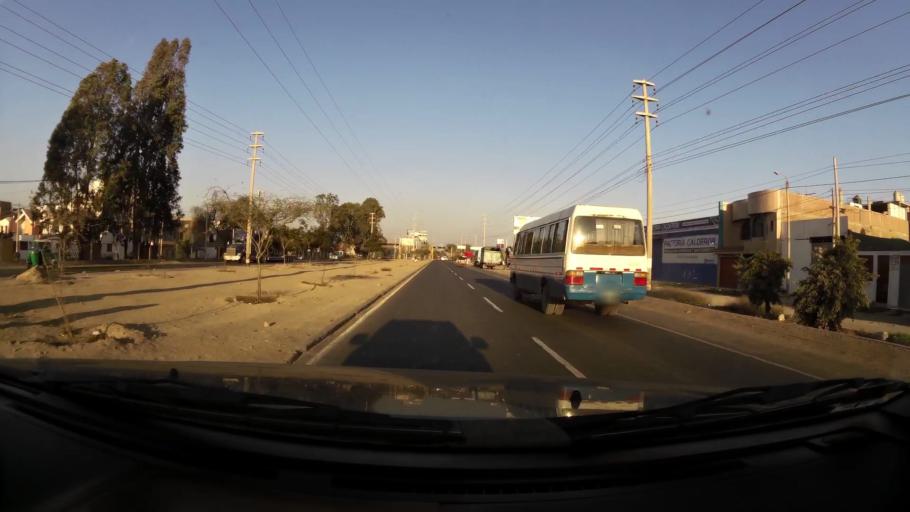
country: PE
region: Ica
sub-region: Provincia de Ica
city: Ica
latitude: -14.0878
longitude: -75.7257
